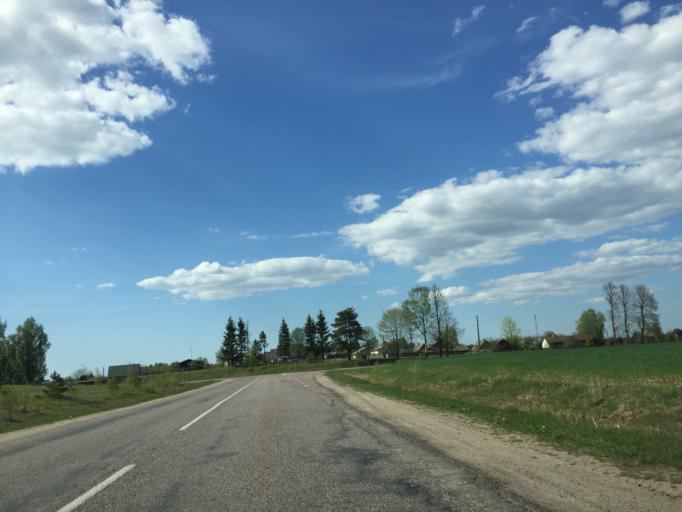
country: LV
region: Limbazu Rajons
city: Limbazi
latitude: 57.5127
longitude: 24.8144
